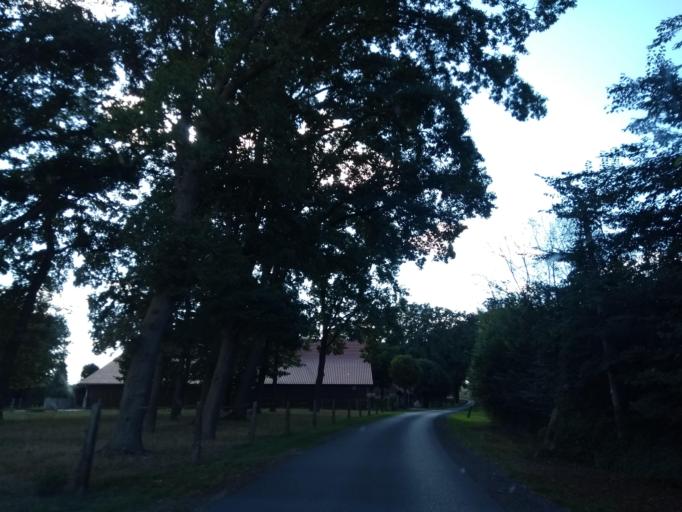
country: DE
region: North Rhine-Westphalia
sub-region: Regierungsbezirk Detmold
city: Delbruck
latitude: 51.7476
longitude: 8.4900
